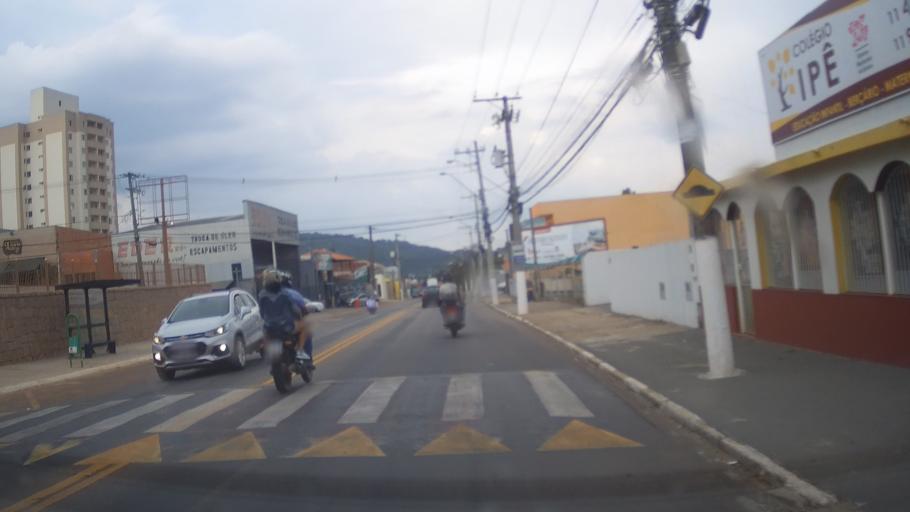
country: BR
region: Sao Paulo
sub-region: Itupeva
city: Itupeva
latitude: -23.1640
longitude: -47.0553
